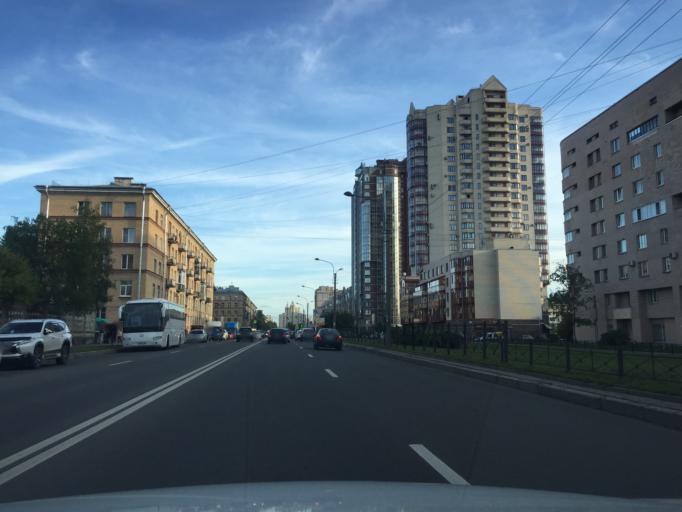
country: RU
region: St.-Petersburg
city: Kupchino
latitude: 59.8540
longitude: 30.3146
